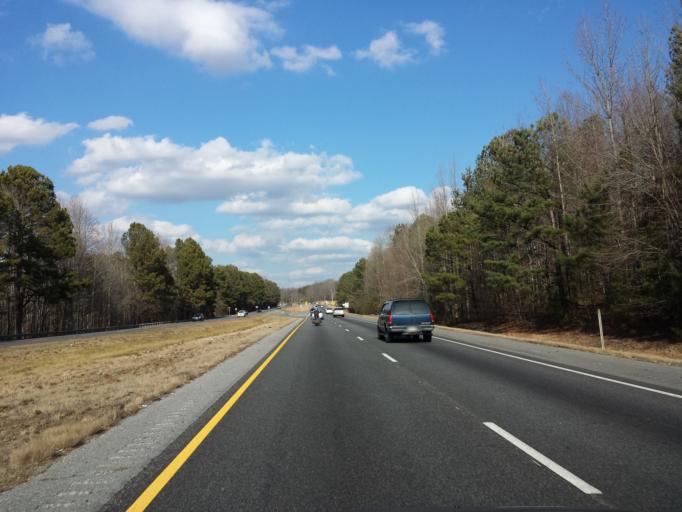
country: US
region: Georgia
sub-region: Forsyth County
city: Cumming
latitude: 34.2660
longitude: -84.0842
